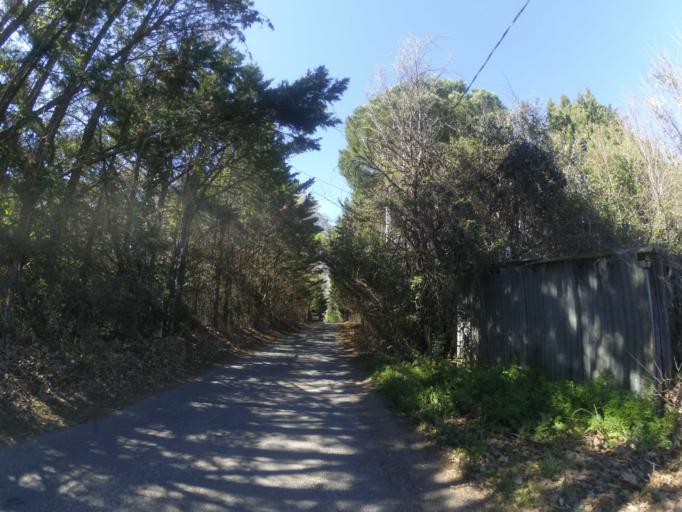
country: FR
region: Languedoc-Roussillon
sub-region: Departement des Pyrenees-Orientales
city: Toulouges
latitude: 42.6735
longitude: 2.8196
